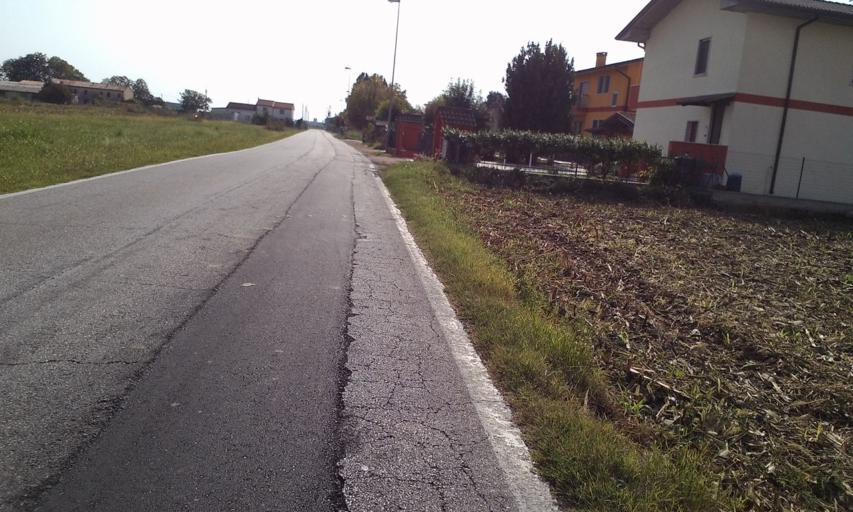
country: IT
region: Veneto
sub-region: Provincia di Verona
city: Povegliano Veronese
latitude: 45.3642
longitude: 10.8923
